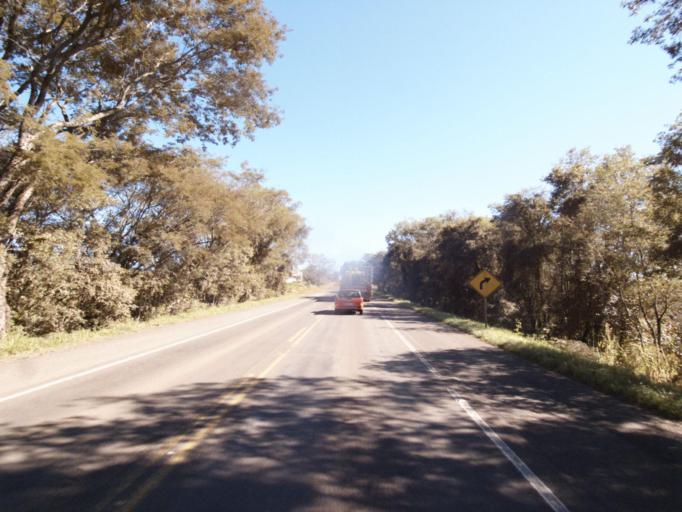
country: AR
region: Misiones
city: Bernardo de Irigoyen
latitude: -26.7697
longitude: -53.4733
